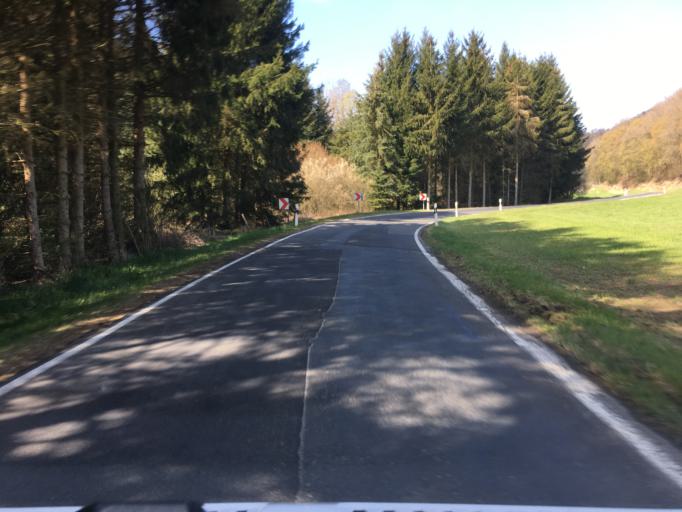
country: DE
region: Rheinland-Pfalz
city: Lind
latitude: 50.5089
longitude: 6.9376
